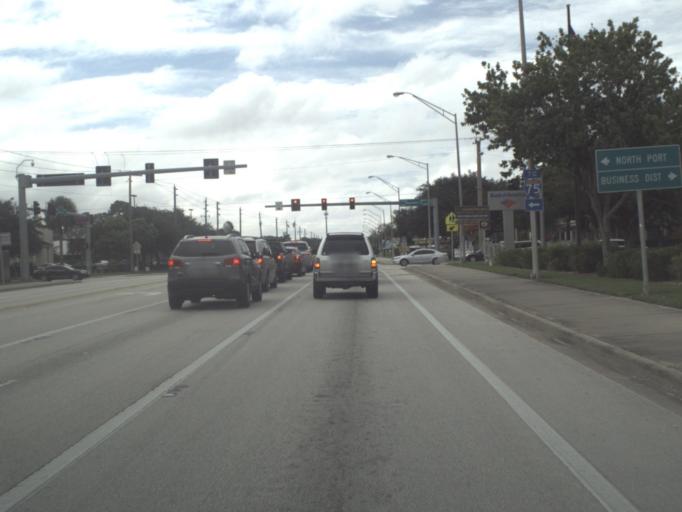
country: US
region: Florida
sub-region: Sarasota County
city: Englewood
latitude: 26.9629
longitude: -82.3531
